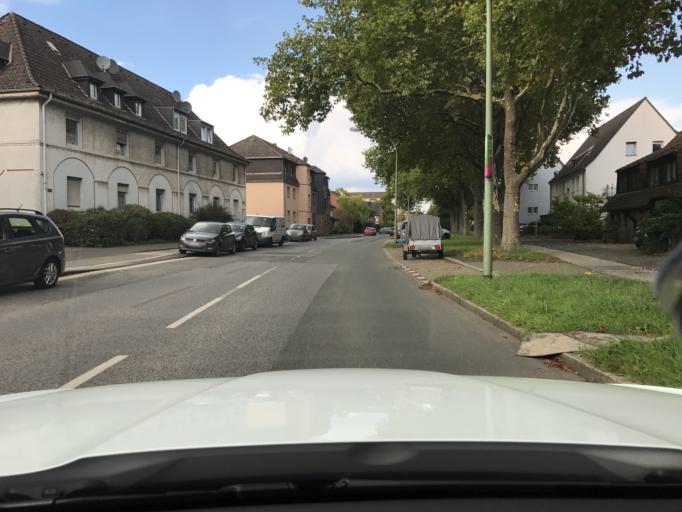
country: DE
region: North Rhine-Westphalia
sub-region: Regierungsbezirk Dusseldorf
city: Hochfeld
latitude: 51.3765
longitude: 6.7432
